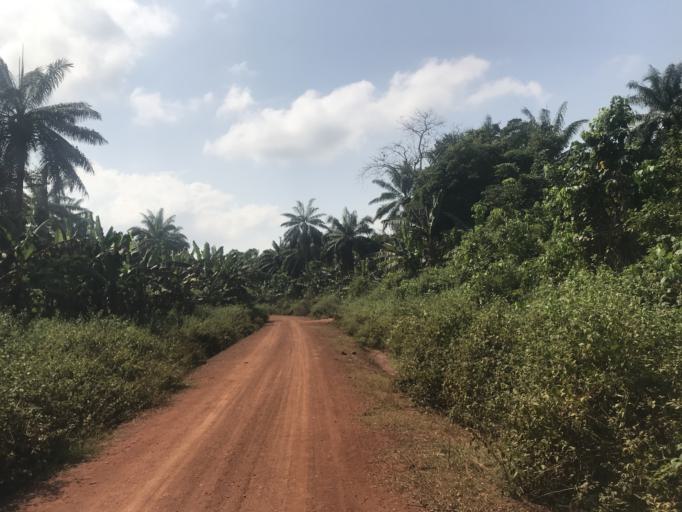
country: NG
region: Osun
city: Ibokun
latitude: 7.8117
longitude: 4.6465
